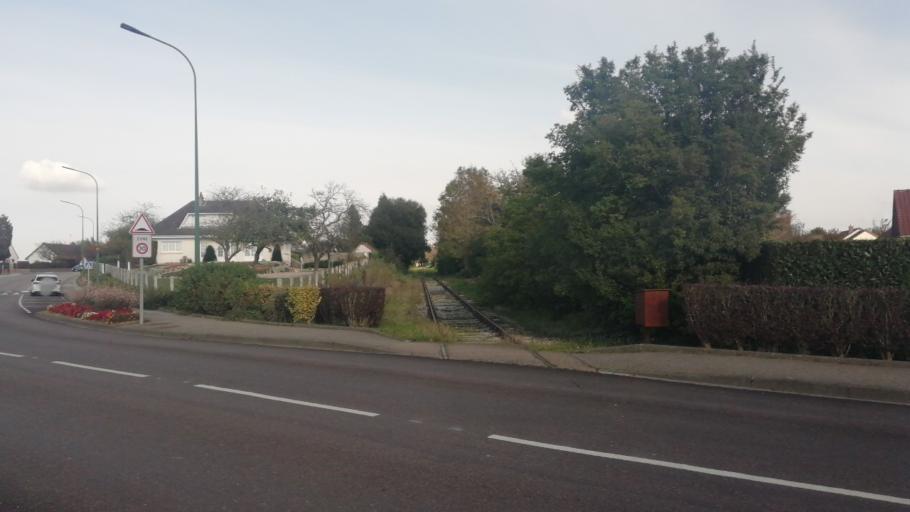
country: FR
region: Haute-Normandie
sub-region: Departement de la Seine-Maritime
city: Gonneville-la-Mallet
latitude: 49.6399
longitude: 0.2635
